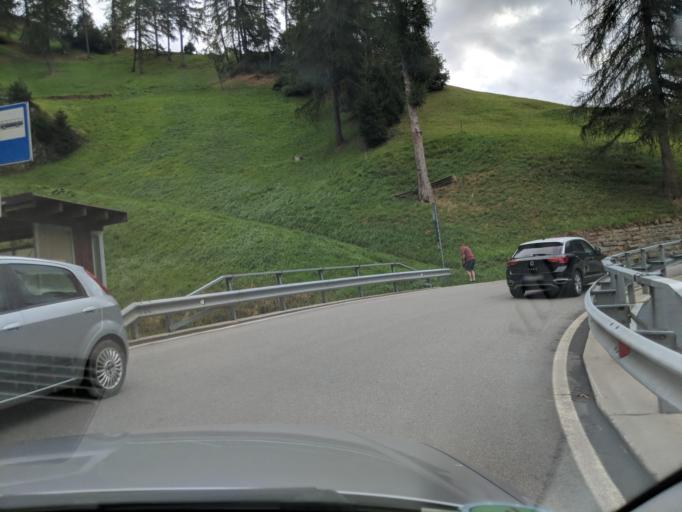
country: IT
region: Trentino-Alto Adige
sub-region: Bolzano
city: Racines
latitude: 46.8268
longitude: 11.2870
